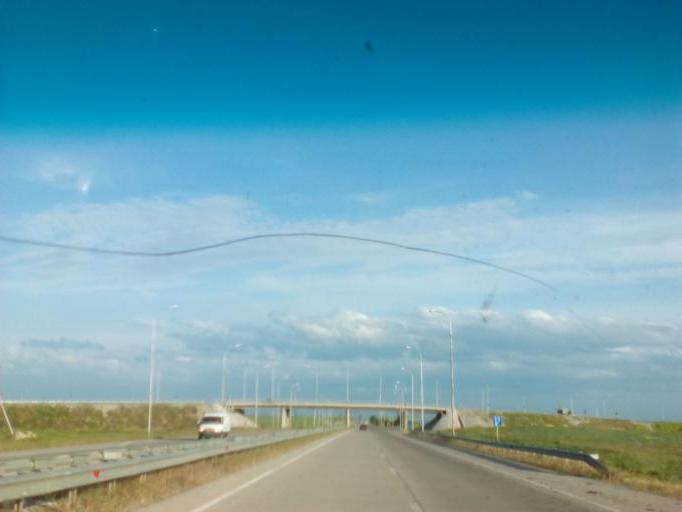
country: KZ
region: Ongtustik Qazaqstan
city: Temirlanovka
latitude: 42.5504
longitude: 69.3212
